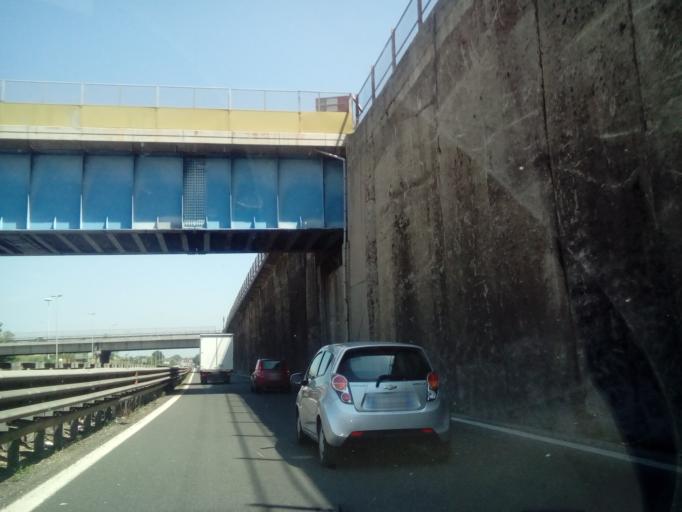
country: IT
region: Latium
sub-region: Citta metropolitana di Roma Capitale
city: Setteville
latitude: 41.8920
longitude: 12.6154
